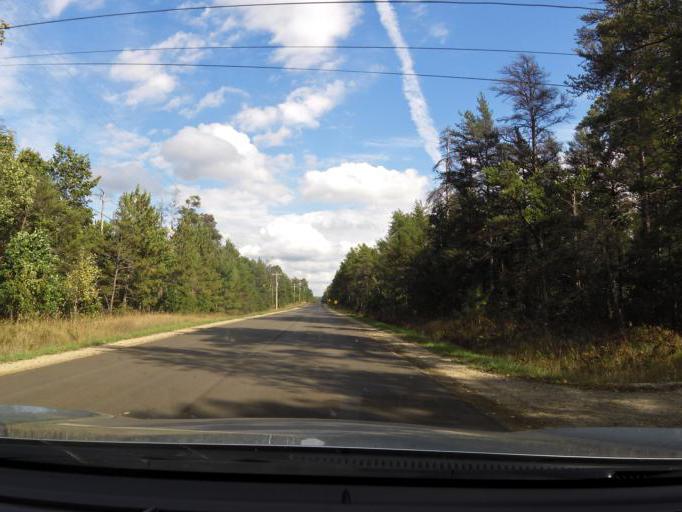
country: US
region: Michigan
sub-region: Roscommon County
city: Roscommon
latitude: 44.5255
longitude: -84.5557
